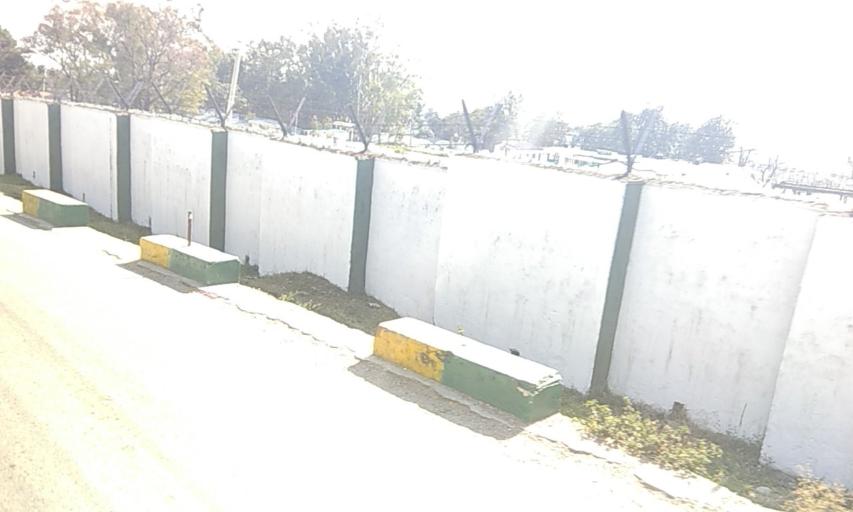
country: IN
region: Himachal Pradesh
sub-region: Kangra
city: Dharmsala
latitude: 32.1755
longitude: 76.3819
